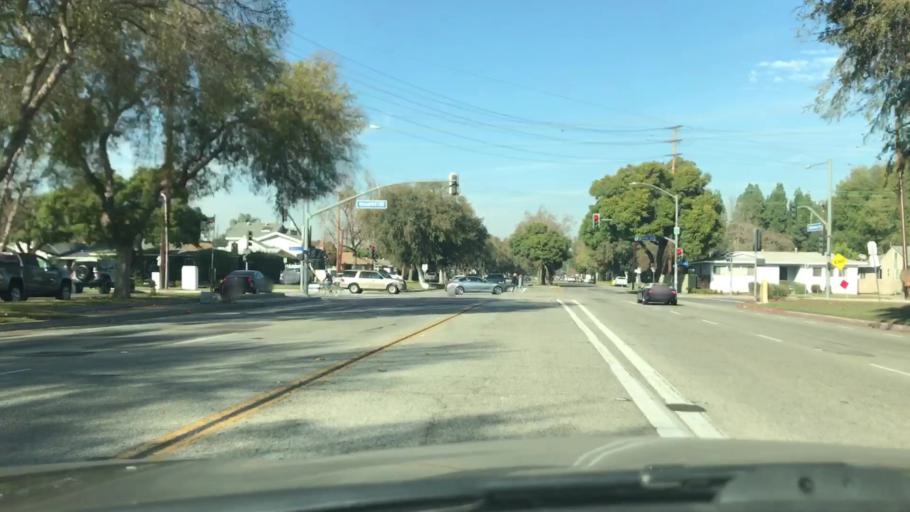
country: US
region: California
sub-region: Orange County
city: Rossmoor
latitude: 33.7950
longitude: -118.0993
